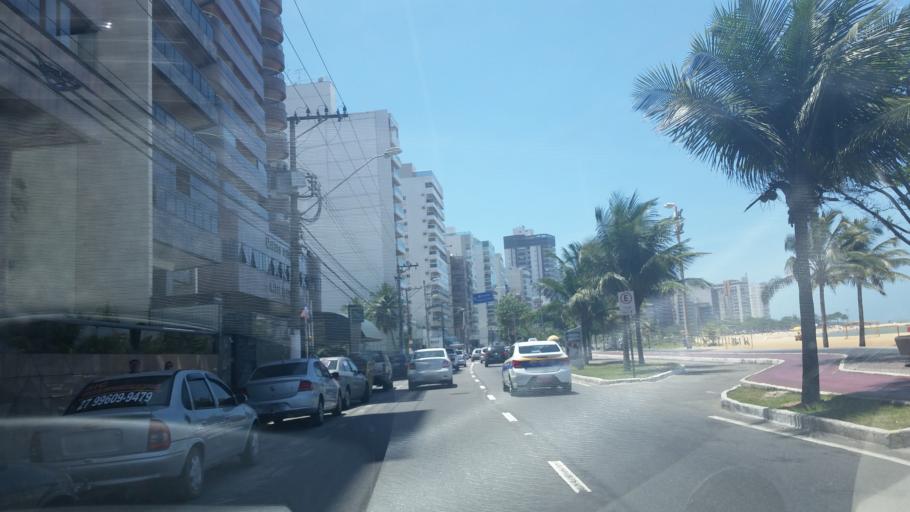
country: BR
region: Espirito Santo
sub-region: Vila Velha
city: Vila Velha
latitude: -20.3356
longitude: -40.2811
